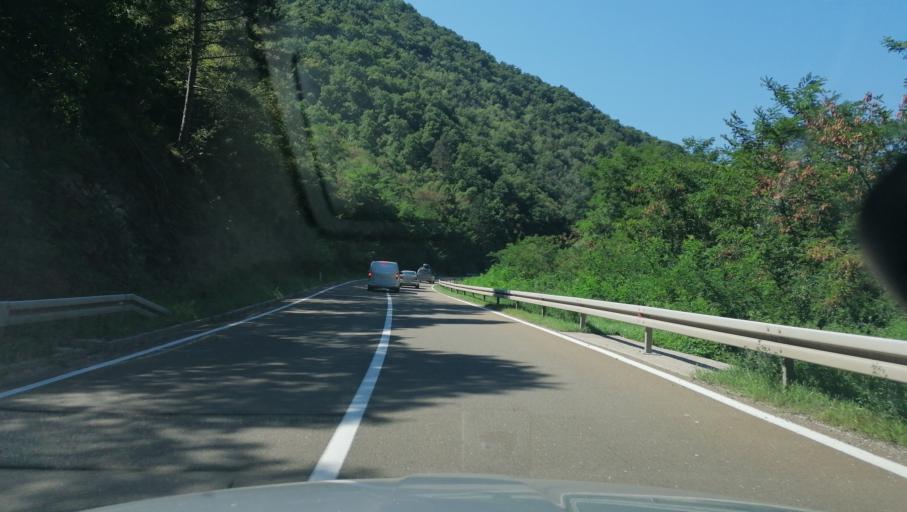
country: RS
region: Central Serbia
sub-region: Raski Okrug
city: Kraljevo
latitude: 43.5755
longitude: 20.5896
